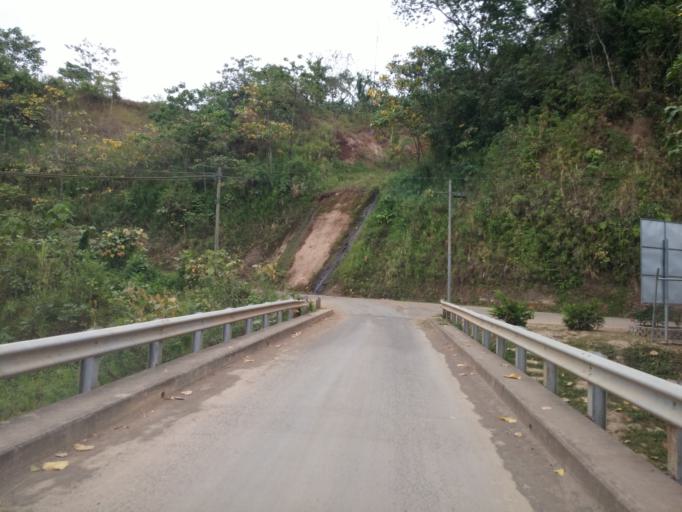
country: CR
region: Alajuela
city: Quesada
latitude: 10.3086
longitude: -84.5240
